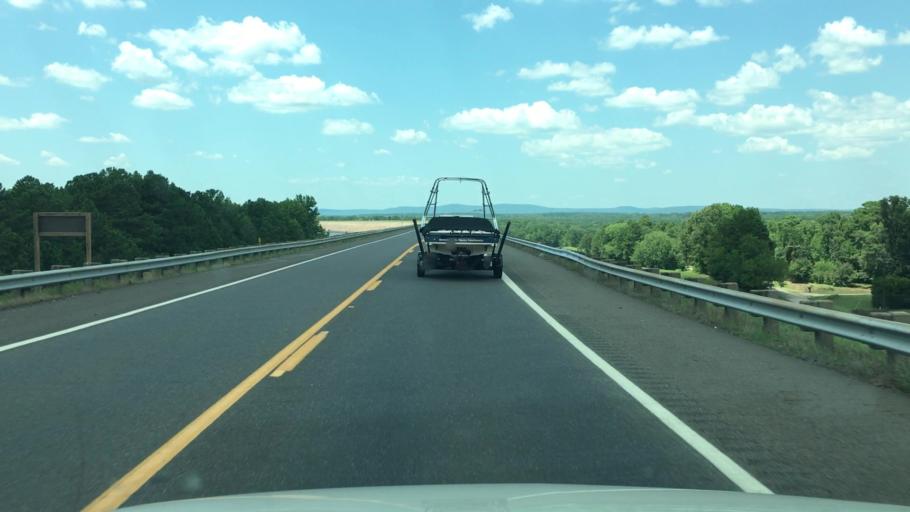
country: US
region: Arkansas
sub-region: Clark County
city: Arkadelphia
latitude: 34.2335
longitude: -93.1005
